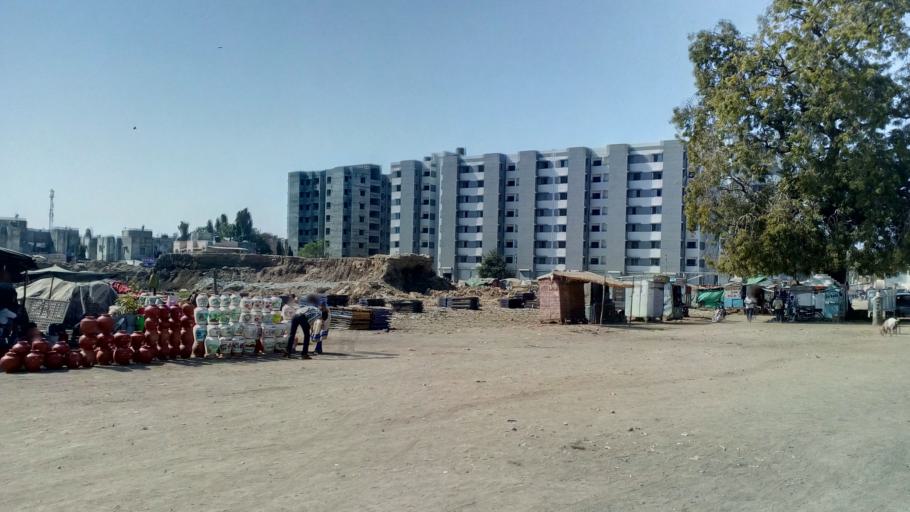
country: IN
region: Punjab
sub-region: Ludhiana
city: Ludhiana
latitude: 30.9390
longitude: 75.8358
